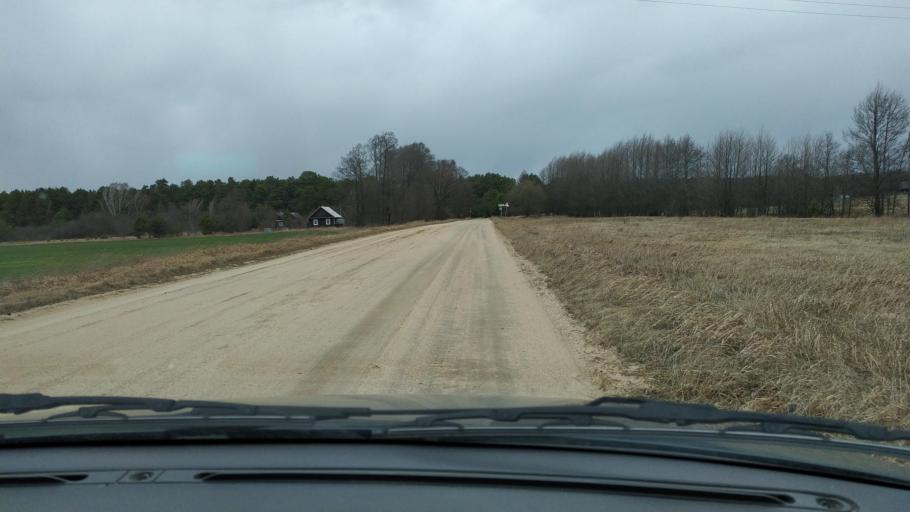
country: BY
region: Brest
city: Kamyanyets
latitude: 52.4093
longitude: 24.0101
